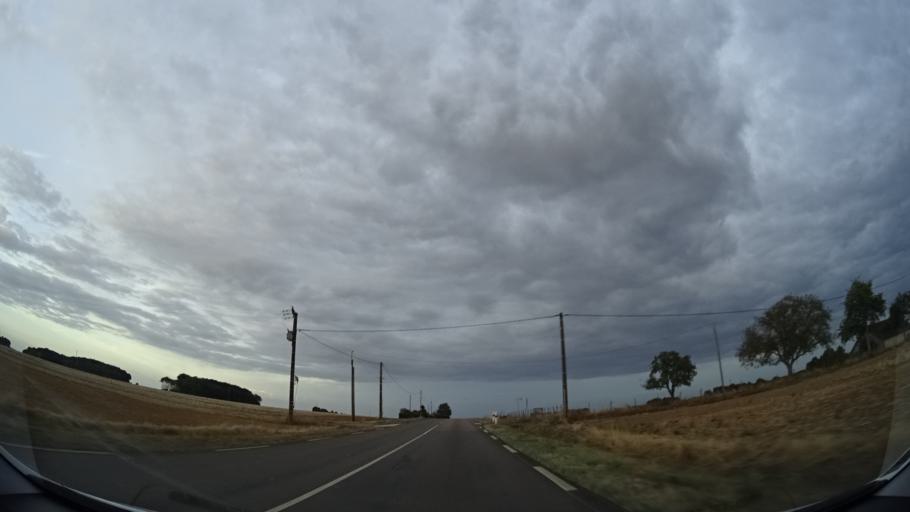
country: FR
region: Bourgogne
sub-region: Departement de l'Yonne
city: Charny
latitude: 47.9325
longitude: 3.1688
